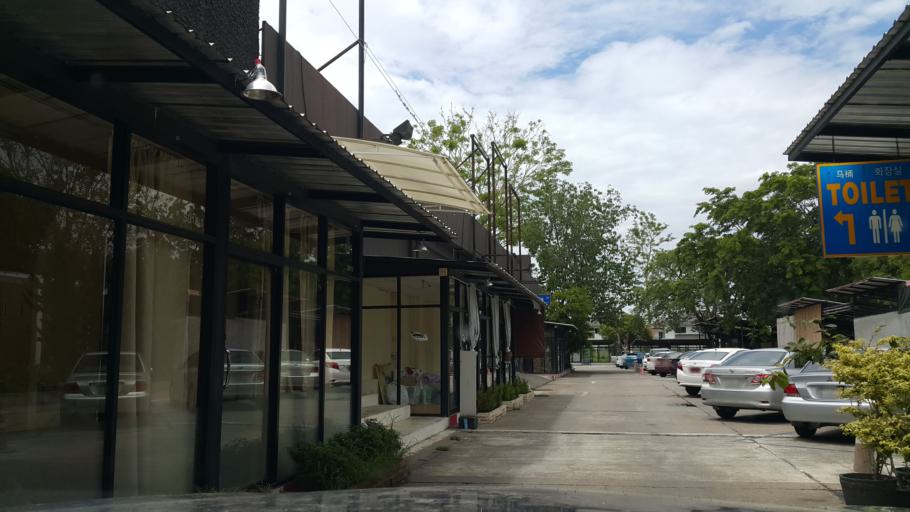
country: TH
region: Chiang Mai
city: Chiang Mai
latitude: 18.7821
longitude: 99.0307
